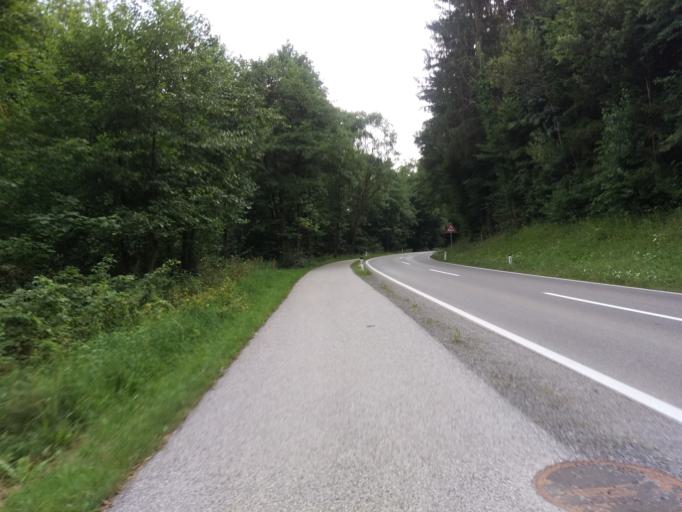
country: AT
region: Styria
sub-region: Politischer Bezirk Graz-Umgebung
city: Thal
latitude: 47.0852
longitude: 15.3706
